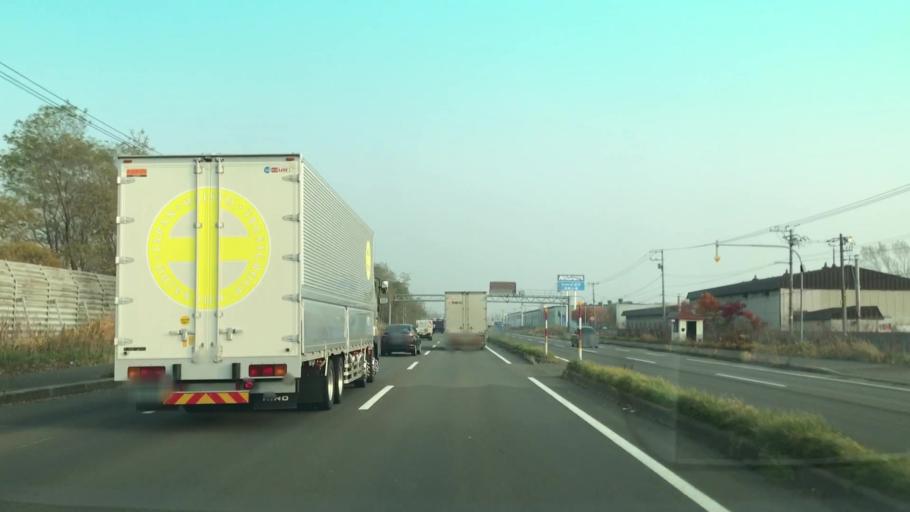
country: JP
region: Hokkaido
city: Ishikari
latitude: 43.1895
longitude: 141.3256
